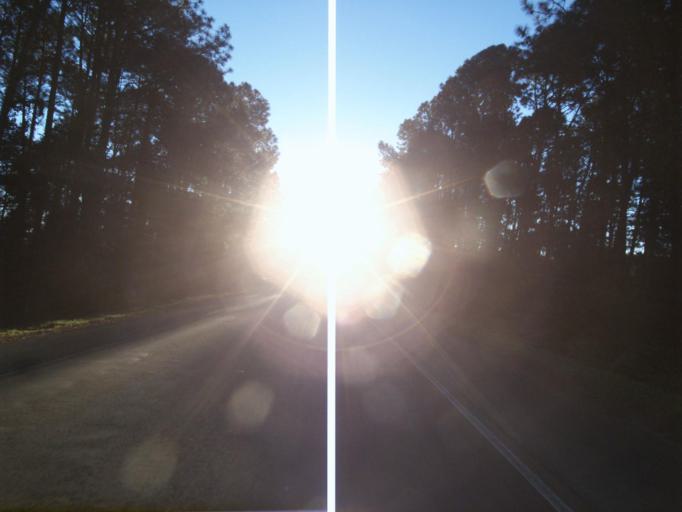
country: BR
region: Santa Catarina
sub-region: Sao Lourenco Do Oeste
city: Sao Lourenco dOeste
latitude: -26.8078
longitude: -53.1714
